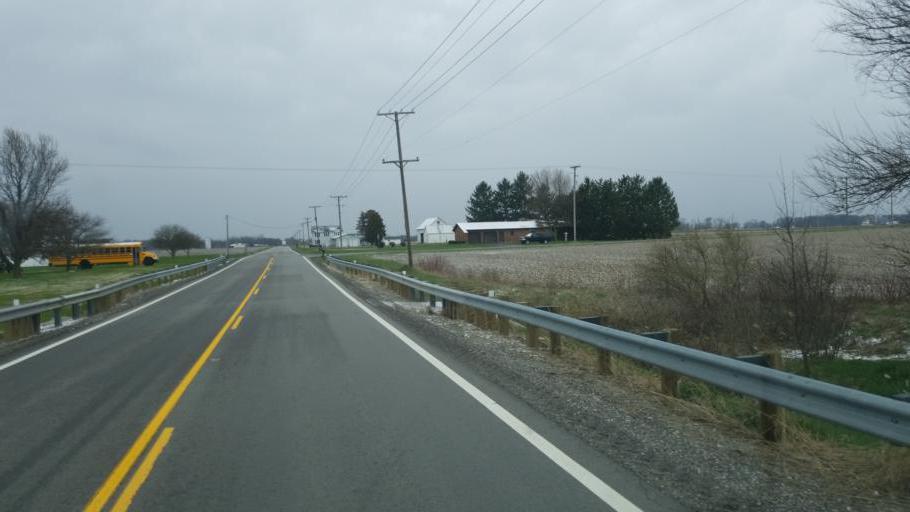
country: US
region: Ohio
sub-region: Marion County
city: Marion
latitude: 40.4851
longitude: -83.0686
